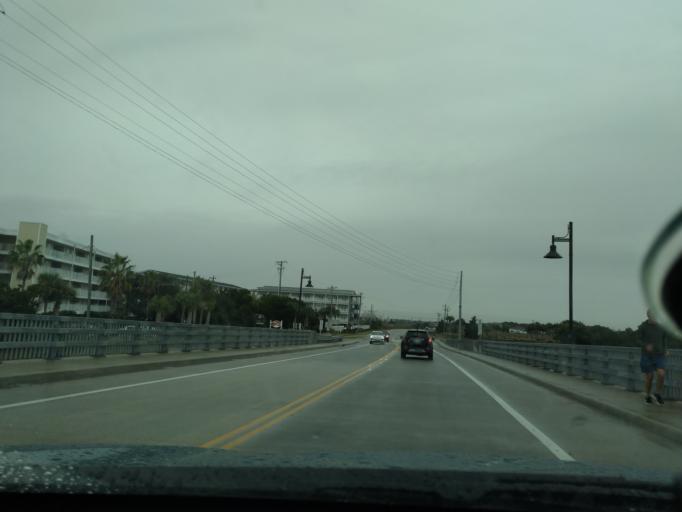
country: US
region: South Carolina
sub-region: Charleston County
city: Folly Beach
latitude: 32.6623
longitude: -79.9438
